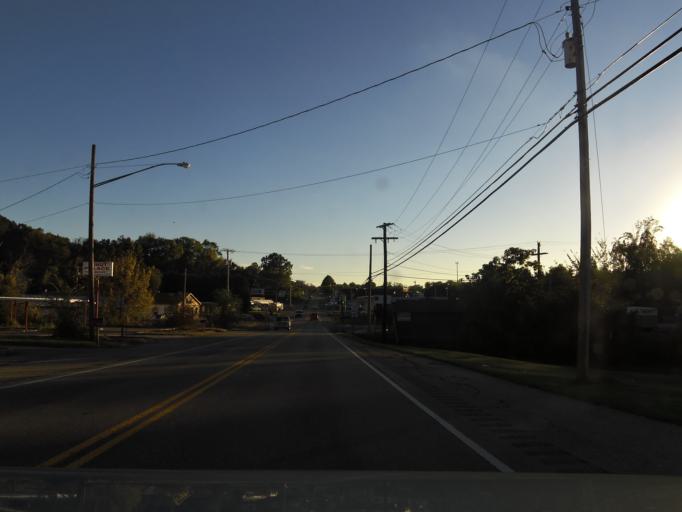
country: US
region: Tennessee
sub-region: Blount County
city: Alcoa
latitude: 35.7768
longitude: -83.9531
